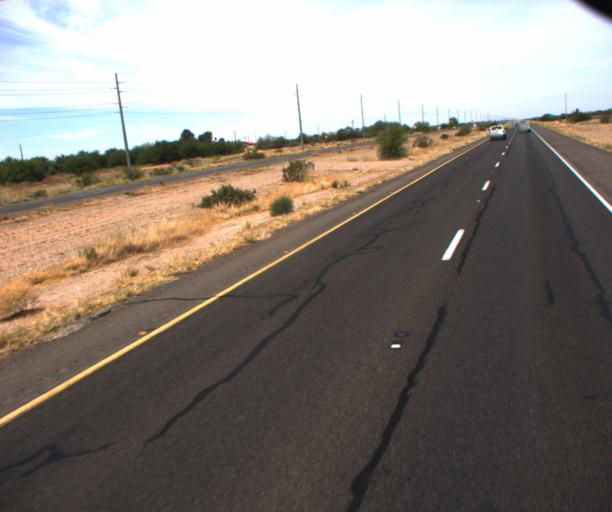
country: US
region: Arizona
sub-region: Maricopa County
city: Sun City West
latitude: 33.7096
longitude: -112.4409
